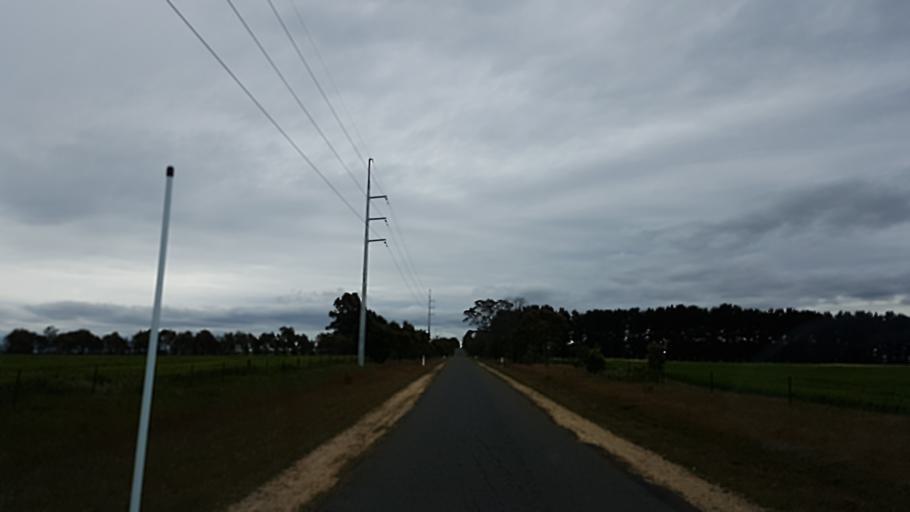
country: AU
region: Victoria
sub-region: Ballarat North
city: Mount Clear
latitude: -37.7788
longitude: 143.9803
